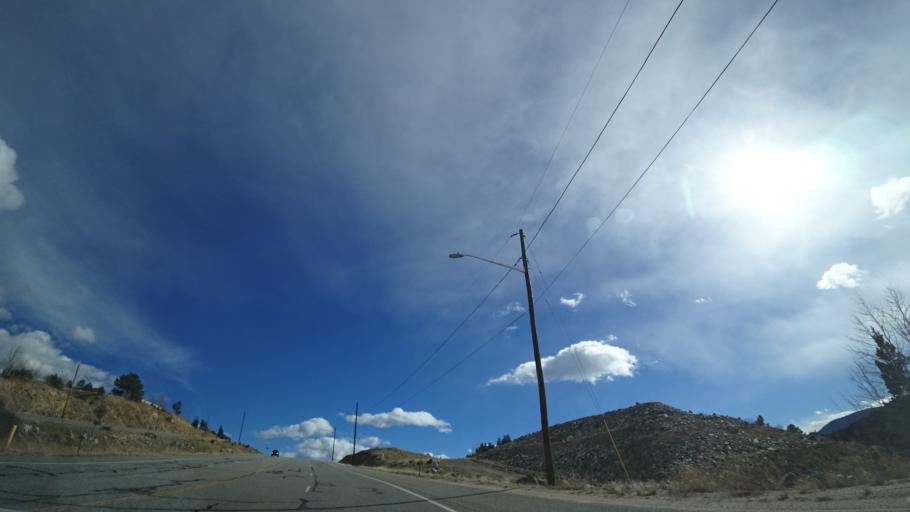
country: US
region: Colorado
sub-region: Gilpin County
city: Central City
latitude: 39.7899
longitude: -105.5151
